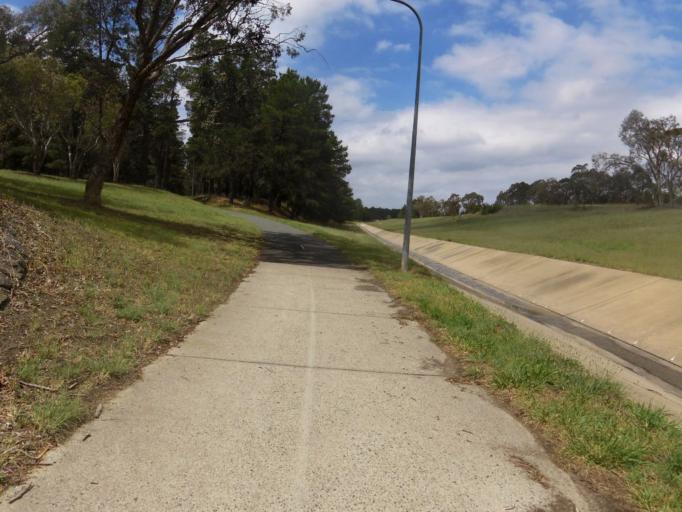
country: AU
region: Australian Capital Territory
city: Macarthur
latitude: -35.4157
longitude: 149.1142
